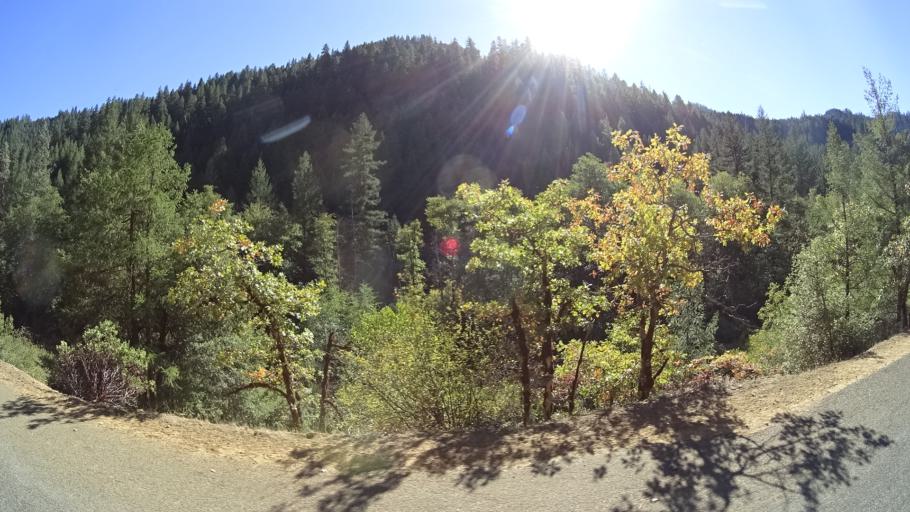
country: US
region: California
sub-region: Siskiyou County
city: Happy Camp
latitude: 41.3024
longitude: -123.1563
